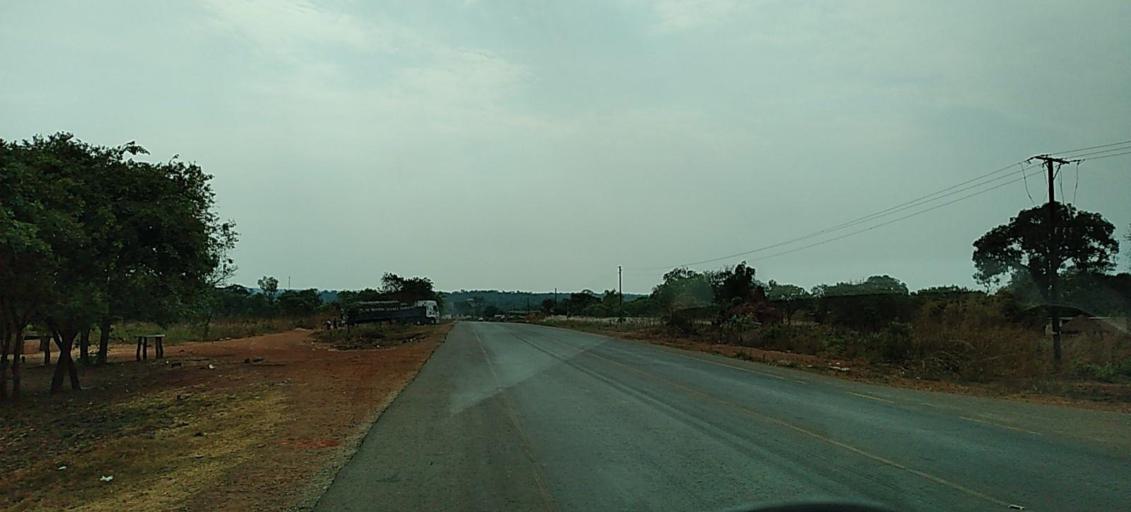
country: ZM
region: North-Western
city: Solwezi
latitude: -12.2019
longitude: 26.4946
